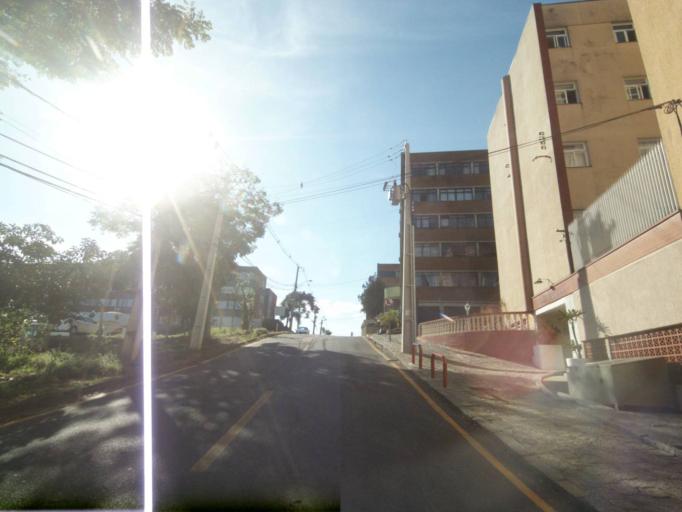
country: BR
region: Parana
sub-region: Curitiba
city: Curitiba
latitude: -25.4365
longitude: -49.2440
